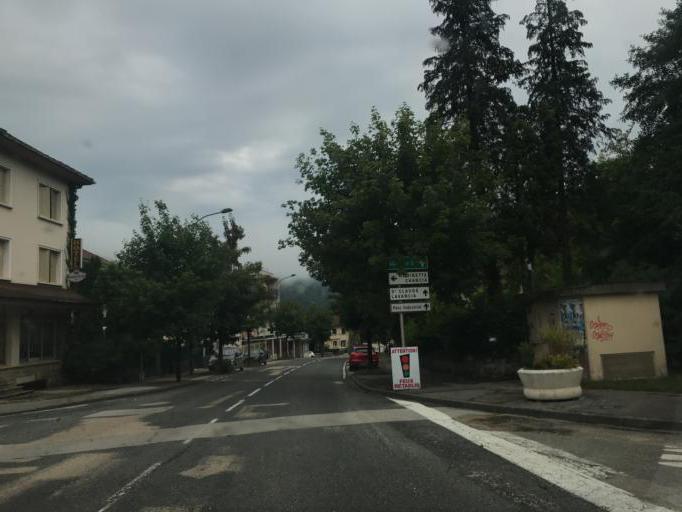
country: FR
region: Rhone-Alpes
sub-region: Departement de l'Ain
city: Dortan
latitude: 46.3172
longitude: 5.6586
